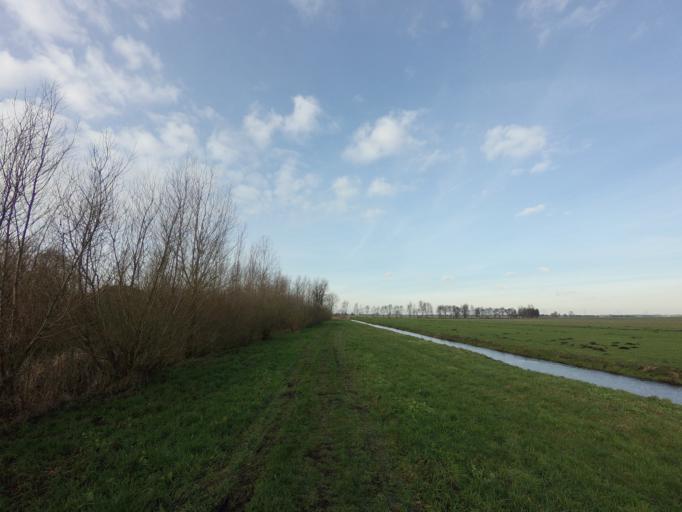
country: NL
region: Utrecht
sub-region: Gemeente Oudewater
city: Oudewater
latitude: 52.0376
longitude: 4.8692
